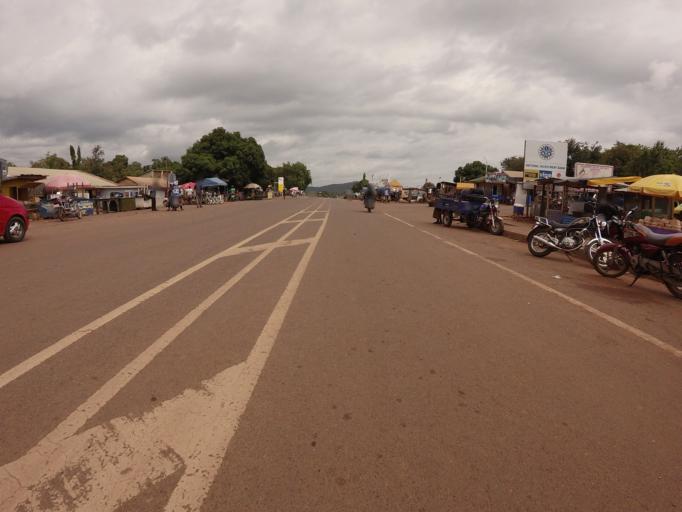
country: TG
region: Centrale
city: Sotouboua
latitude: 8.2602
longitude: 0.5218
